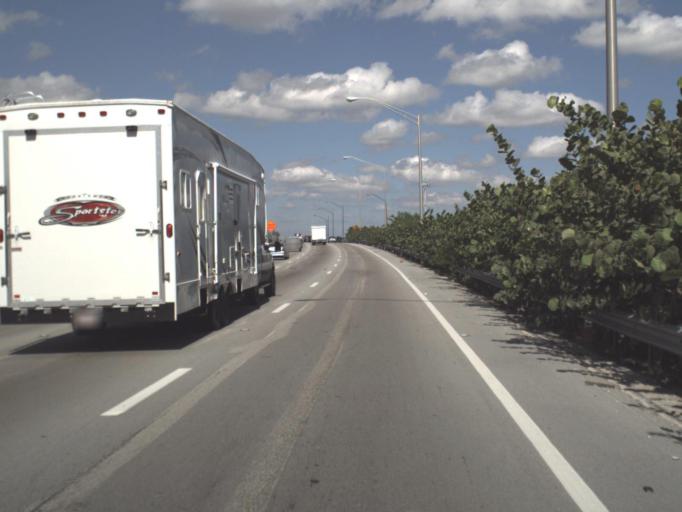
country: US
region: Florida
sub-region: Miami-Dade County
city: Cutler Ridge
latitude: 25.5795
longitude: -80.3650
